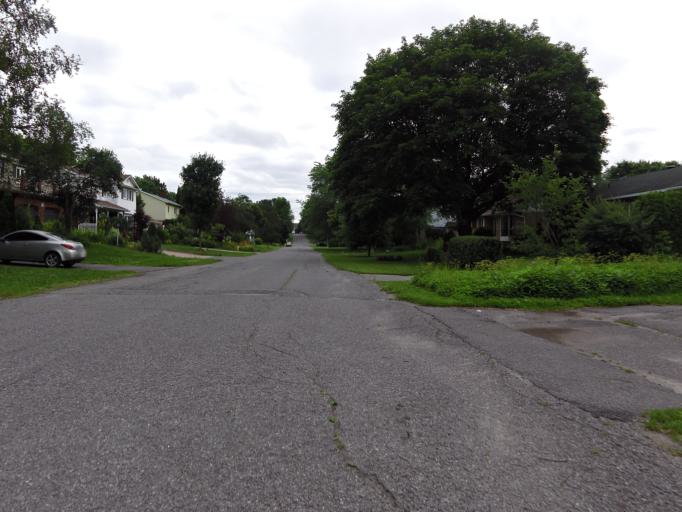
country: CA
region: Ontario
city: Ottawa
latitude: 45.3493
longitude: -75.7443
